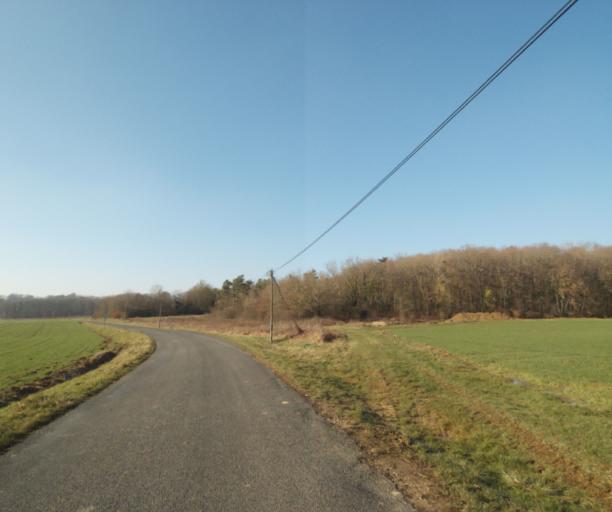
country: FR
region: Champagne-Ardenne
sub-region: Departement de la Haute-Marne
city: Wassy
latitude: 48.5190
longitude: 4.9811
